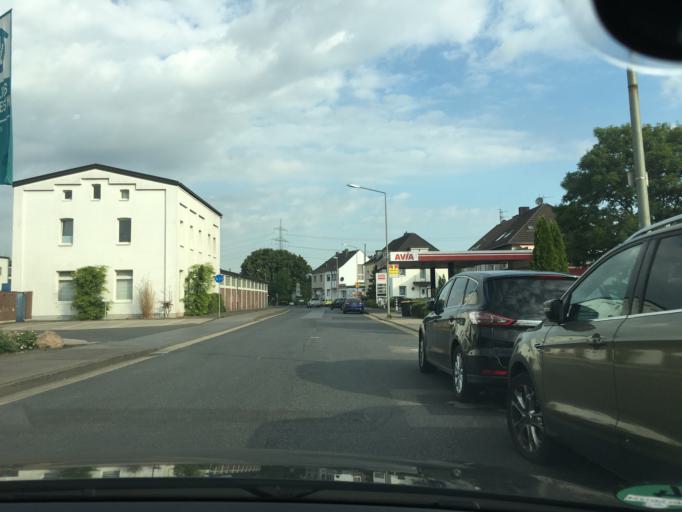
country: DE
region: North Rhine-Westphalia
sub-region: Regierungsbezirk Koln
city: Dueren
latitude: 50.8306
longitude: 6.4441
